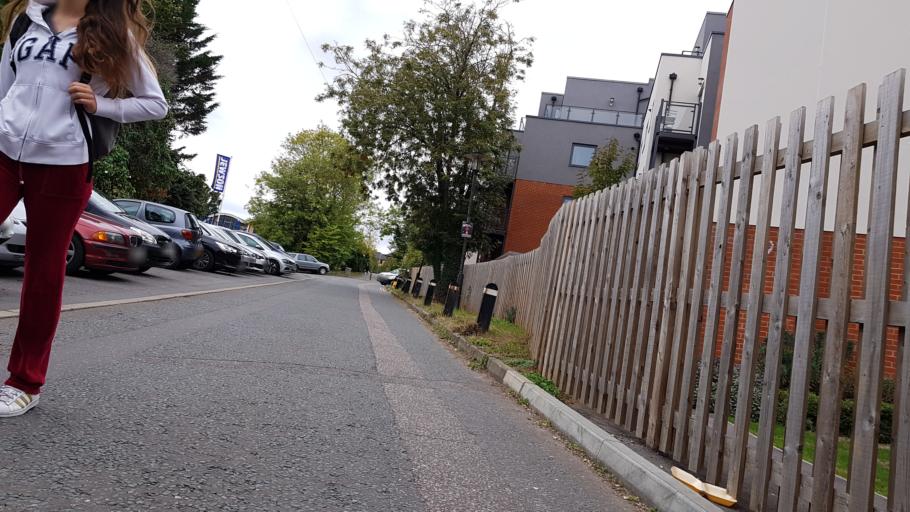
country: GB
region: England
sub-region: Surrey
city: Guildford
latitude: 51.2419
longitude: -0.5813
